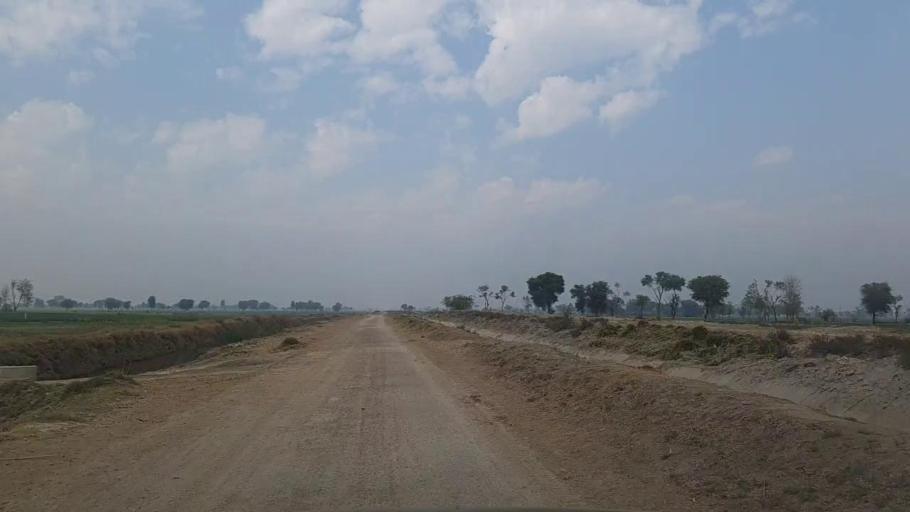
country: PK
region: Sindh
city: Nawabshah
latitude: 26.3636
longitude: 68.4061
